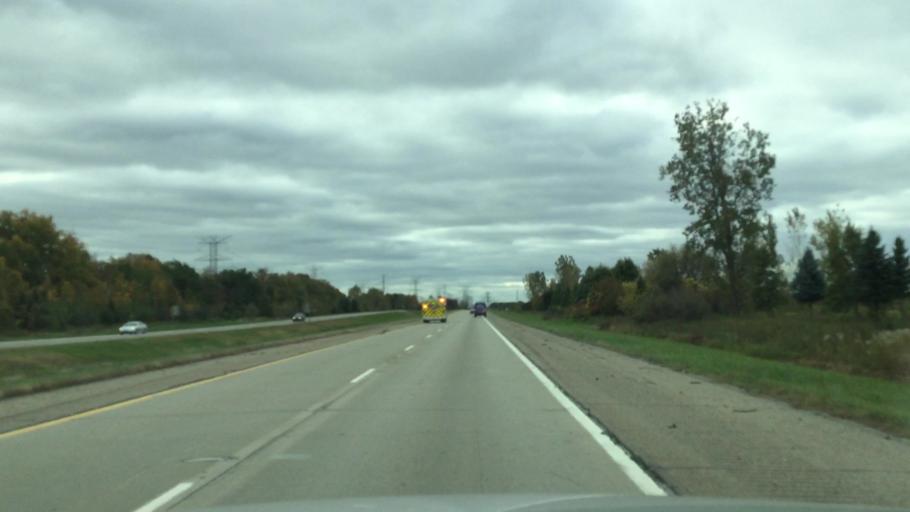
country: US
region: Michigan
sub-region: Macomb County
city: Romeo
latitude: 42.7699
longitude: -83.0094
